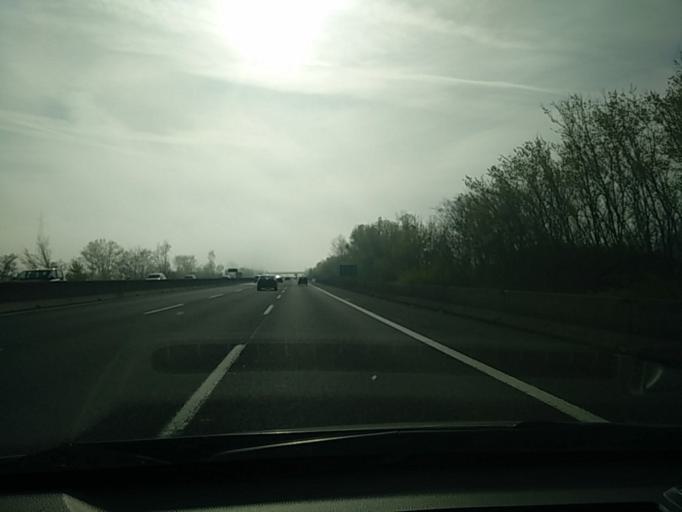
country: IT
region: Emilia-Romagna
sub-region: Provincia di Bologna
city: Osteria Grande
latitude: 44.4580
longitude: 11.5156
